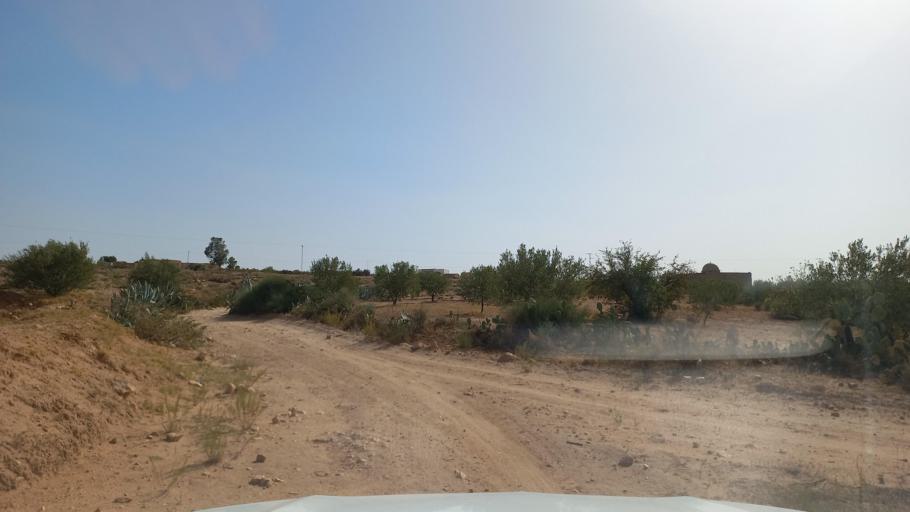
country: TN
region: Al Qasrayn
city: Kasserine
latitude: 35.2086
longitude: 8.9759
